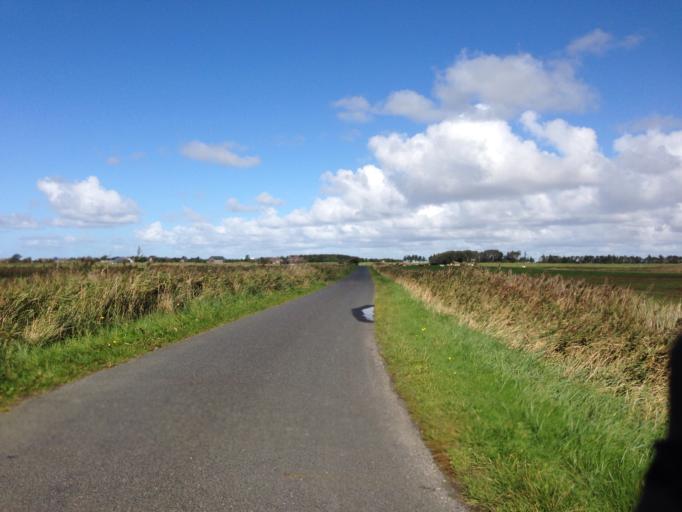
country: DE
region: Schleswig-Holstein
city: Witsum
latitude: 54.6973
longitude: 8.4268
